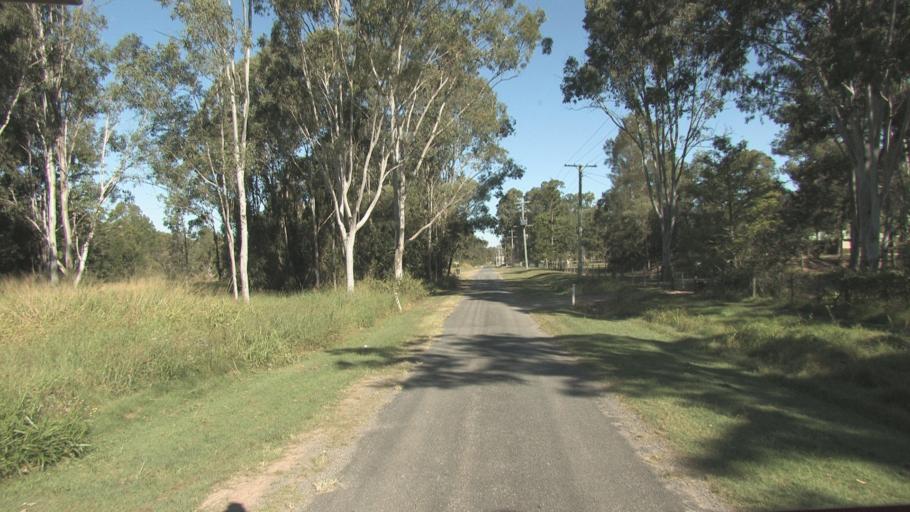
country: AU
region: Queensland
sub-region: Logan
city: Waterford West
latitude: -27.7196
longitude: 153.1259
